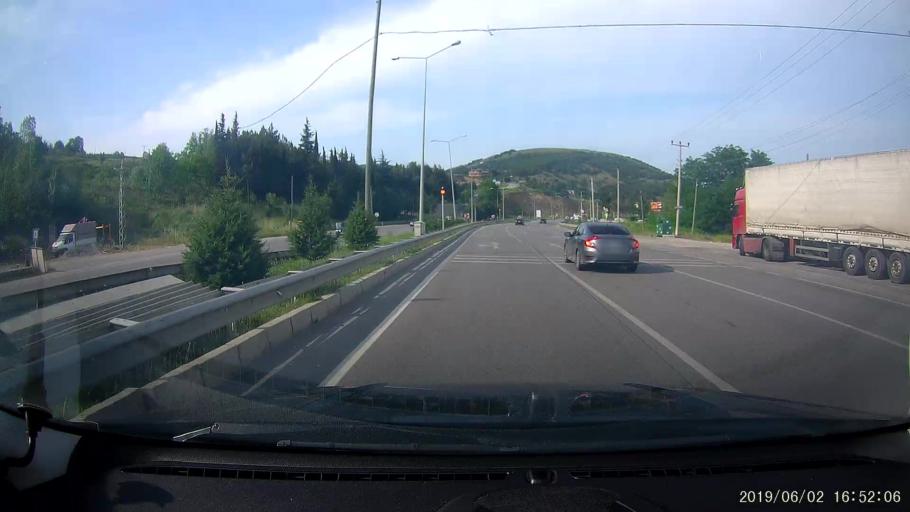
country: TR
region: Samsun
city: Samsun
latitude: 41.2830
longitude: 36.1920
